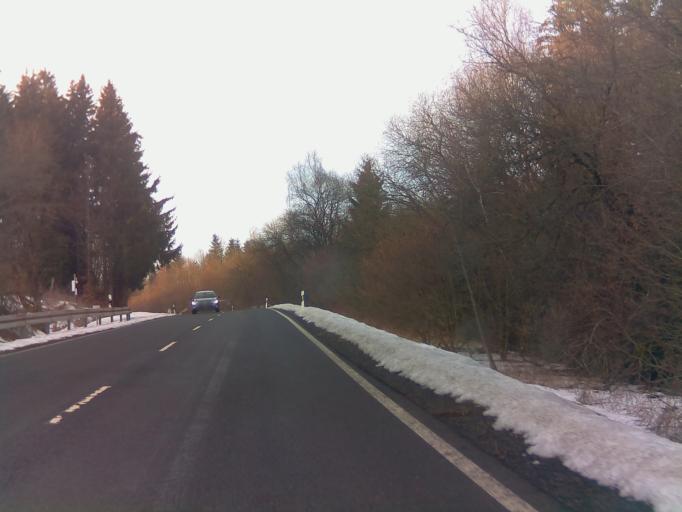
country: DE
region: Bavaria
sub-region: Regierungsbezirk Unterfranken
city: Wildflecken
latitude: 50.3607
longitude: 9.9337
